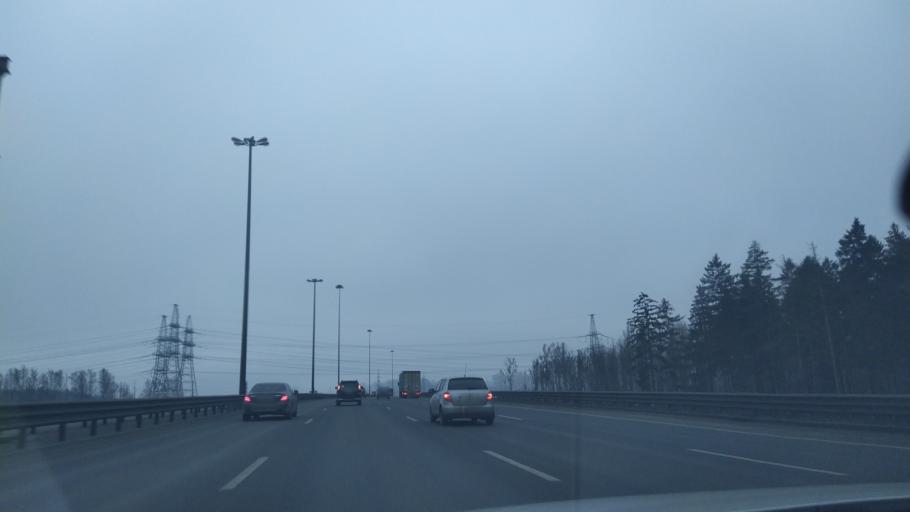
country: RU
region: St.-Petersburg
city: Krasnogvargeisky
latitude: 59.9332
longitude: 30.5376
